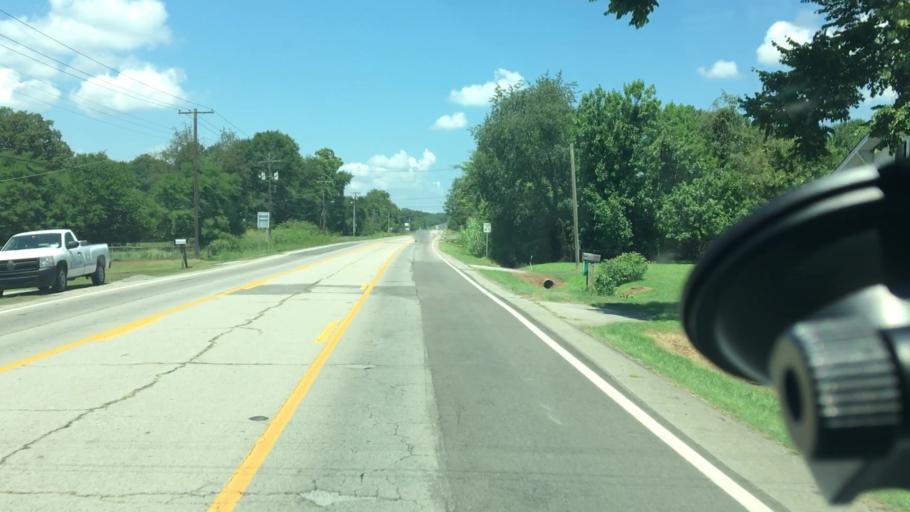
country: US
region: Arkansas
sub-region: Sebastian County
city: Lavaca
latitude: 35.2946
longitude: -94.1417
